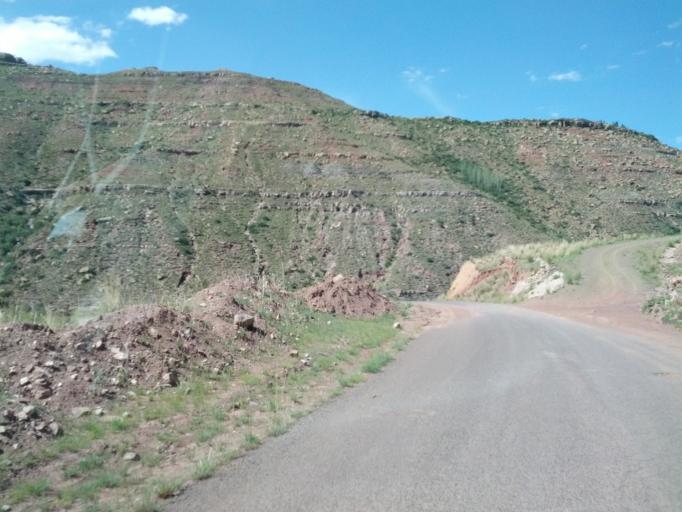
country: LS
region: Qacha's Nek
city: Qacha's Nek
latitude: -30.0691
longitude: 28.4371
